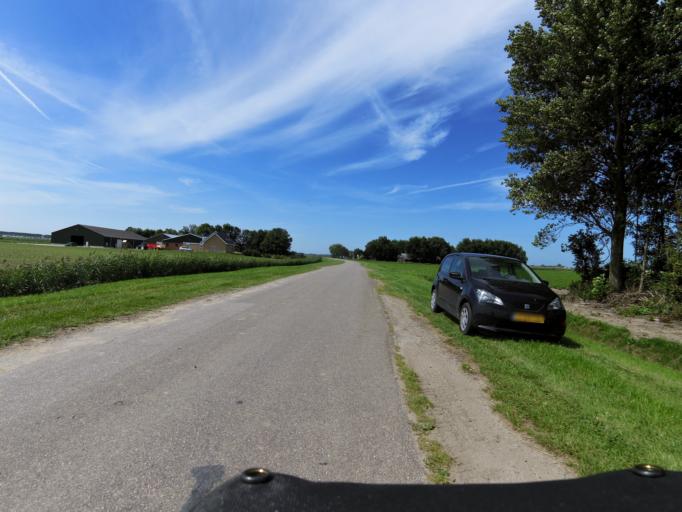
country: NL
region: South Holland
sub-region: Gemeente Goeree-Overflakkee
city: Dirksland
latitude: 51.7982
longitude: 4.0924
